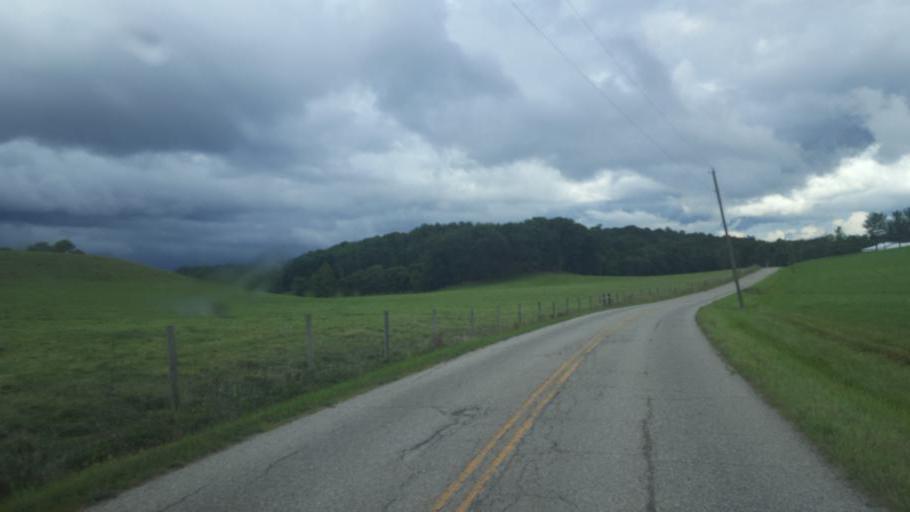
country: US
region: Ohio
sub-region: Jackson County
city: Oak Hill
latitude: 38.9390
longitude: -82.5827
